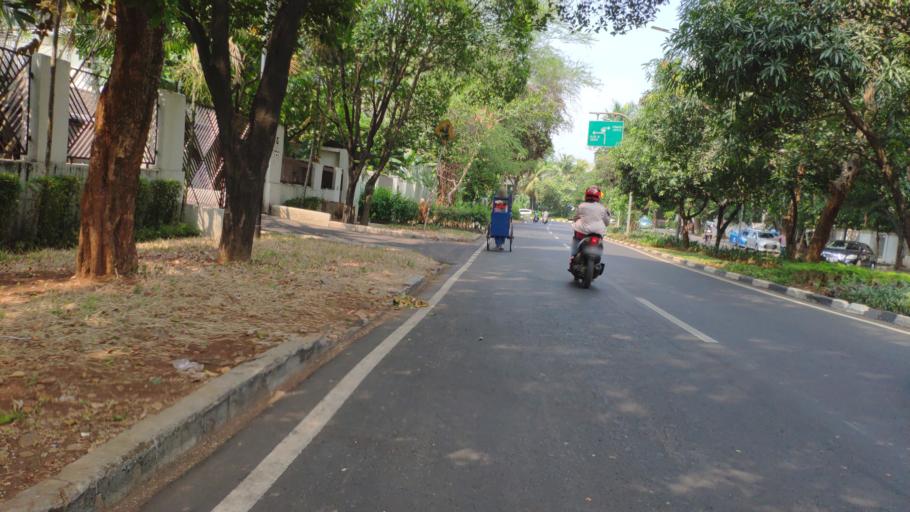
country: ID
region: Jakarta Raya
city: Jakarta
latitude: -6.2506
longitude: 106.8071
